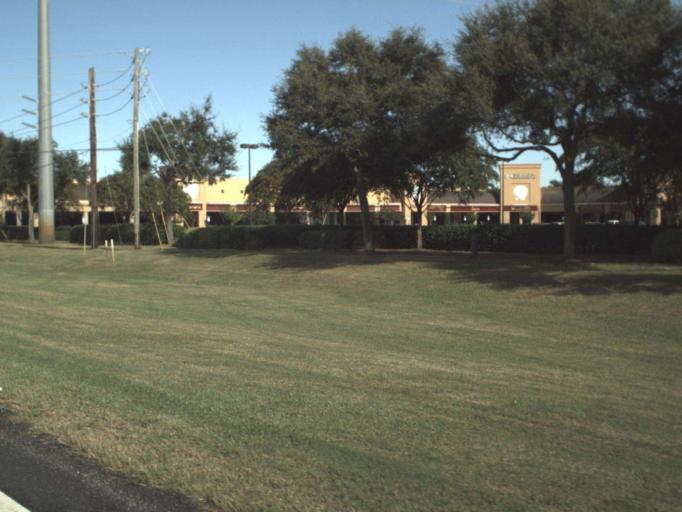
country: US
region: Florida
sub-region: Walton County
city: Miramar Beach
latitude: 30.3792
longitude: -86.3532
